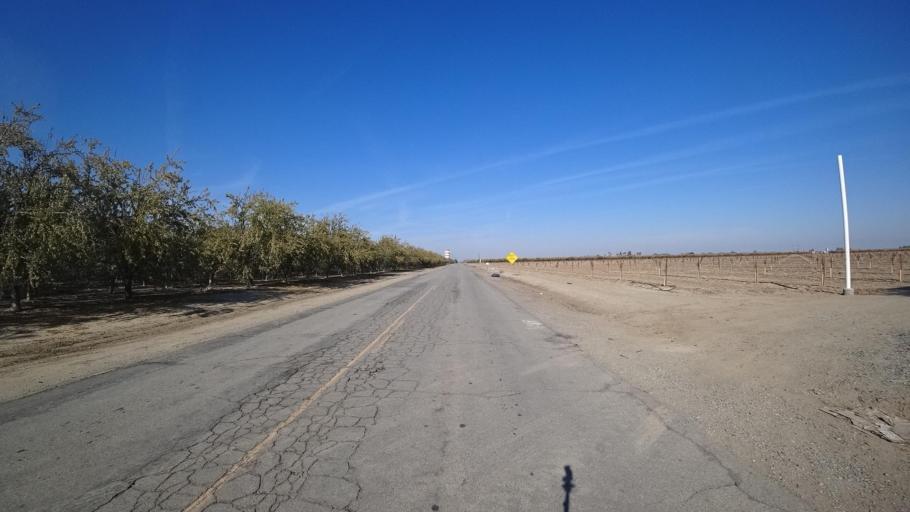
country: US
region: California
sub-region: Kern County
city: Wasco
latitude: 35.6529
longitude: -119.3487
